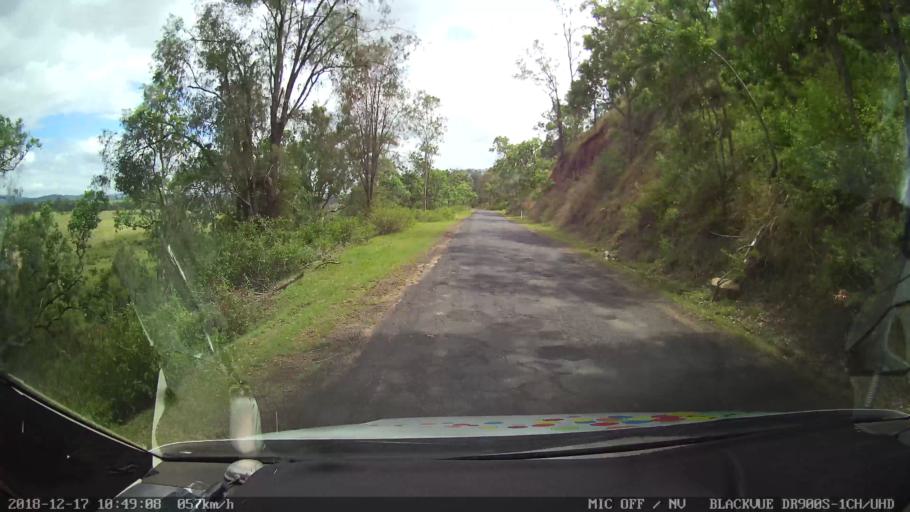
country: AU
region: New South Wales
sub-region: Clarence Valley
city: Gordon
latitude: -28.8679
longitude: 152.5723
